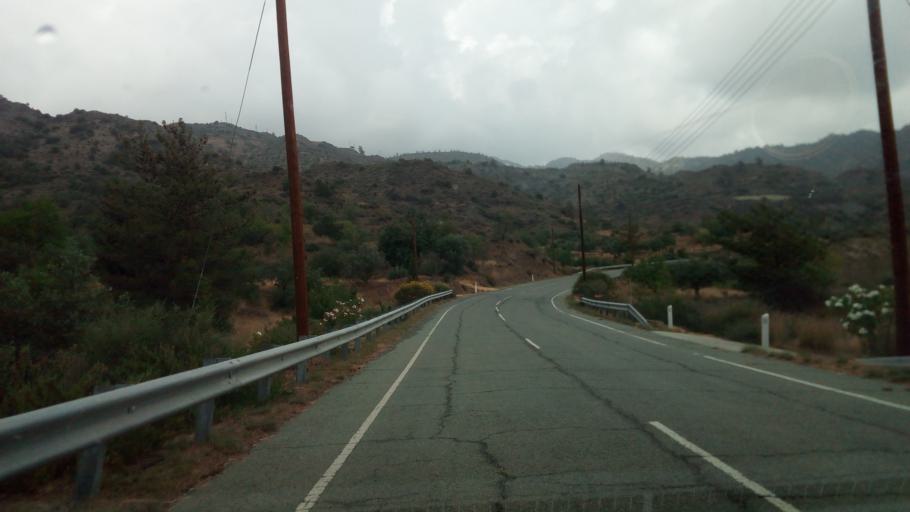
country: CY
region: Limassol
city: Parekklisha
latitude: 34.8676
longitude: 33.1894
